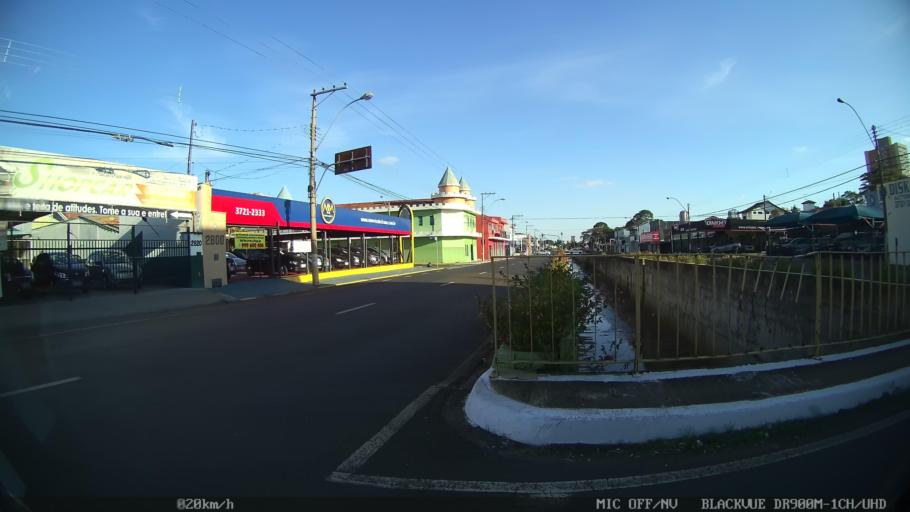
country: BR
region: Sao Paulo
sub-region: Franca
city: Franca
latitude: -20.5288
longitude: -47.4031
